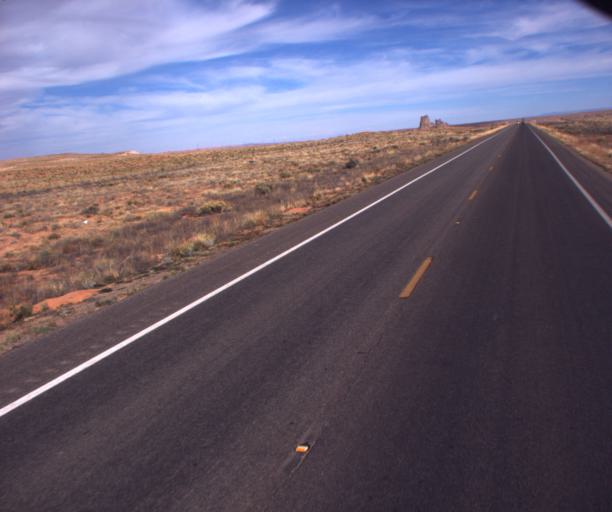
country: US
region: Arizona
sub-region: Navajo County
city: Kayenta
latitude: 36.7190
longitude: -110.1738
